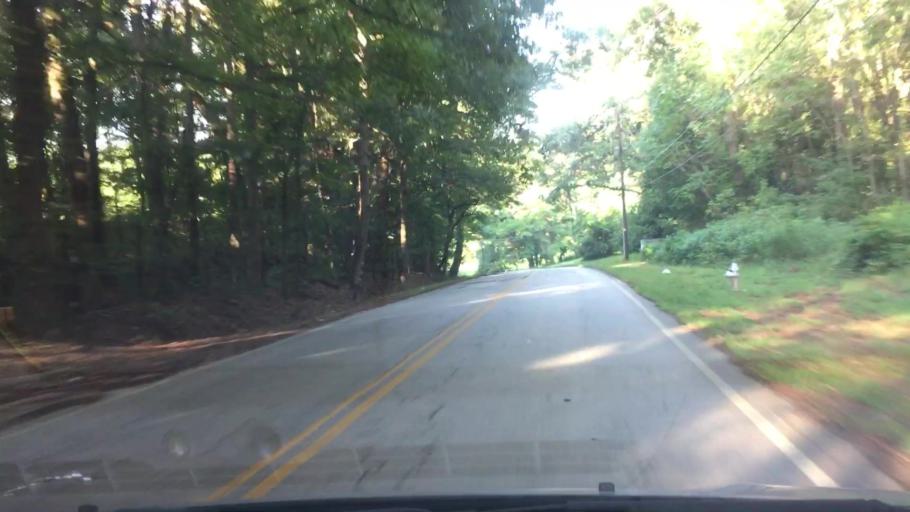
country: US
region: Georgia
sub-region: DeKalb County
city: Gresham Park
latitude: 33.7027
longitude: -84.3302
